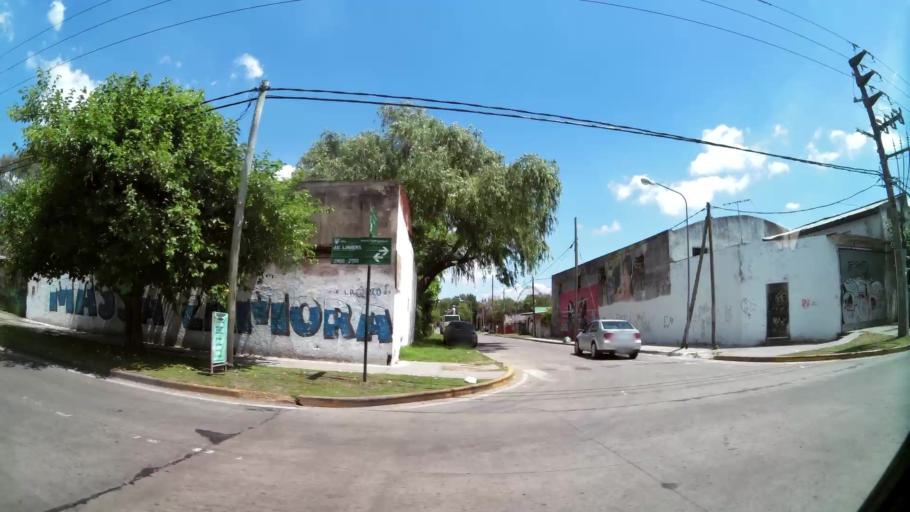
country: AR
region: Buenos Aires
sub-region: Partido de Tigre
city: Tigre
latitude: -34.4366
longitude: -58.5944
